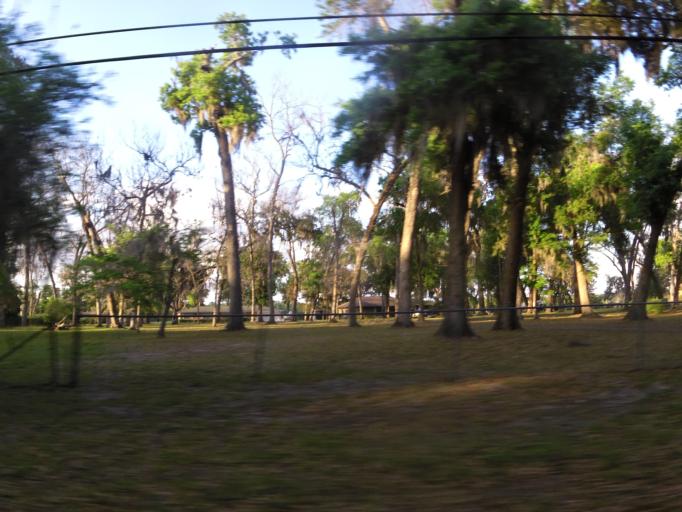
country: US
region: Florida
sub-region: Saint Johns County
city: Fruit Cove
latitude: 30.1274
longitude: -81.6007
